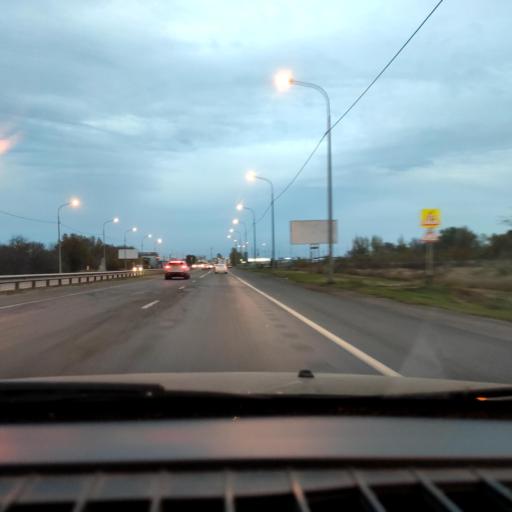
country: RU
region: Samara
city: Tol'yatti
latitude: 53.5731
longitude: 49.4556
